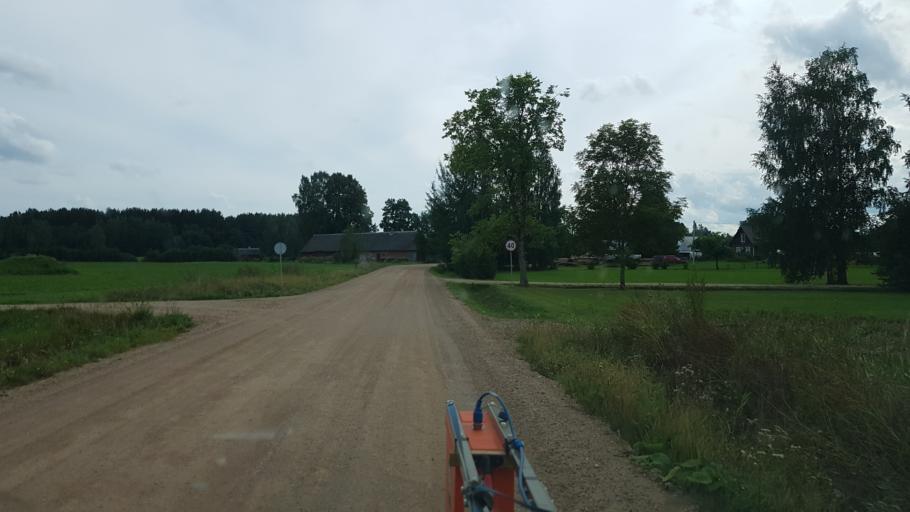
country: RU
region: Pskov
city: Pechory
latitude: 57.7783
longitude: 27.4700
